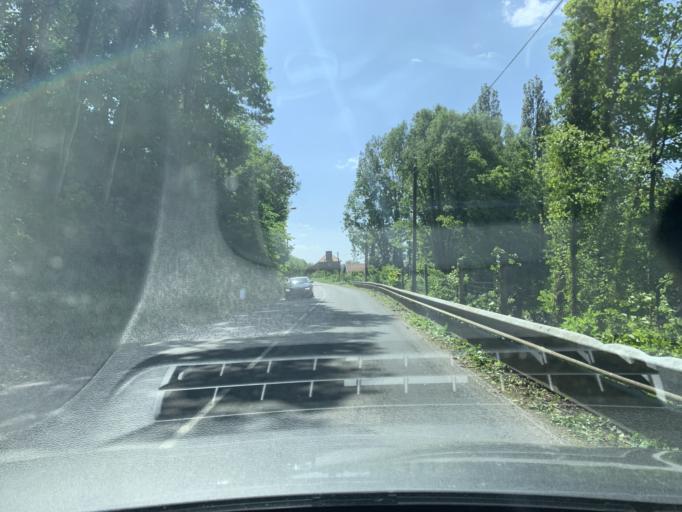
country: FR
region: Nord-Pas-de-Calais
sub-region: Departement du Nord
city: Marcoing
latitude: 50.1247
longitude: 3.1860
